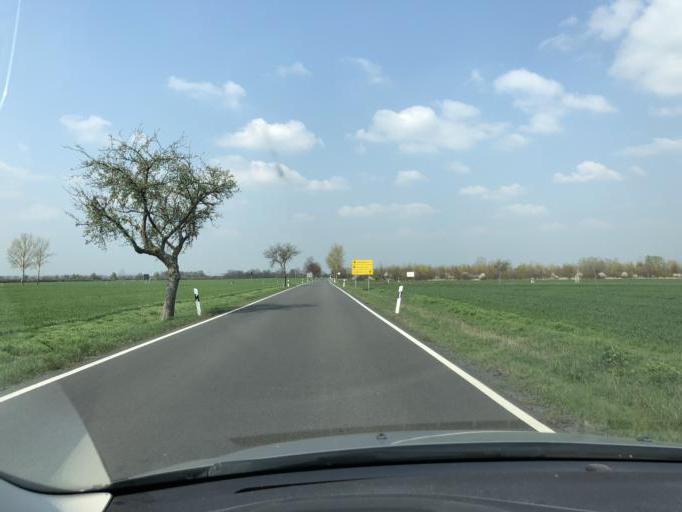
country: DE
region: Saxony
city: Wiedemar
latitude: 51.4935
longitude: 12.2115
